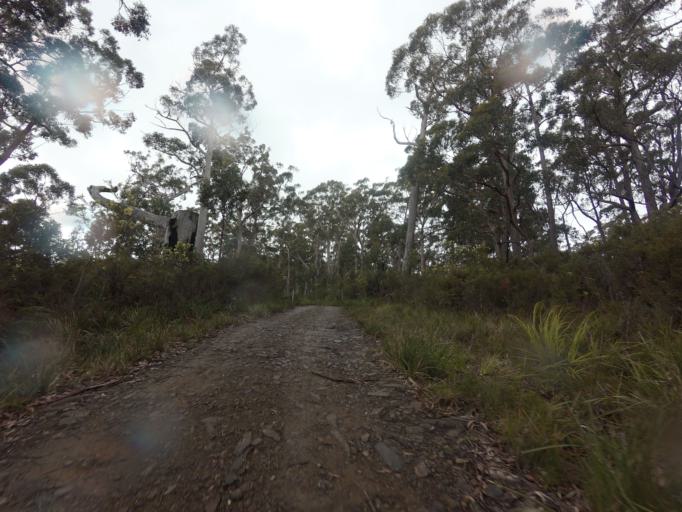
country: AU
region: Tasmania
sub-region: Huon Valley
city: Geeveston
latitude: -43.4650
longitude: 146.9228
